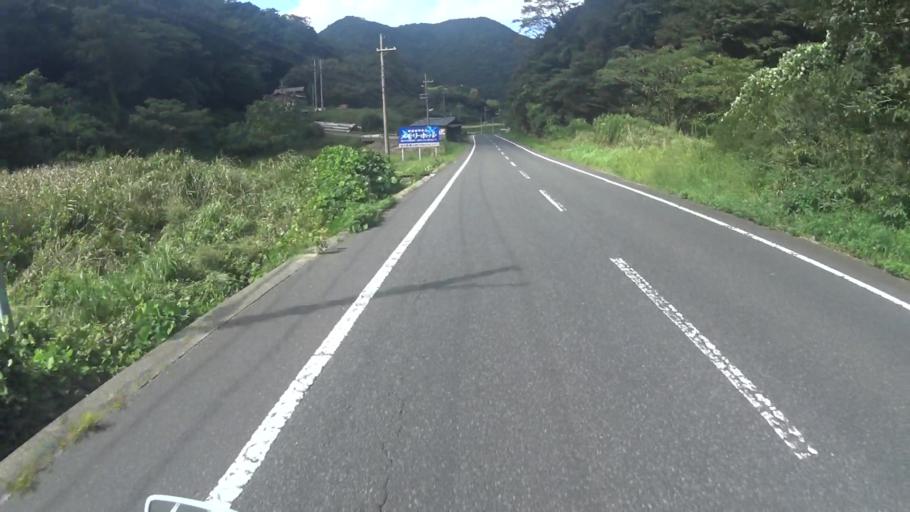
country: JP
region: Kyoto
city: Miyazu
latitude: 35.6903
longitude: 135.2782
